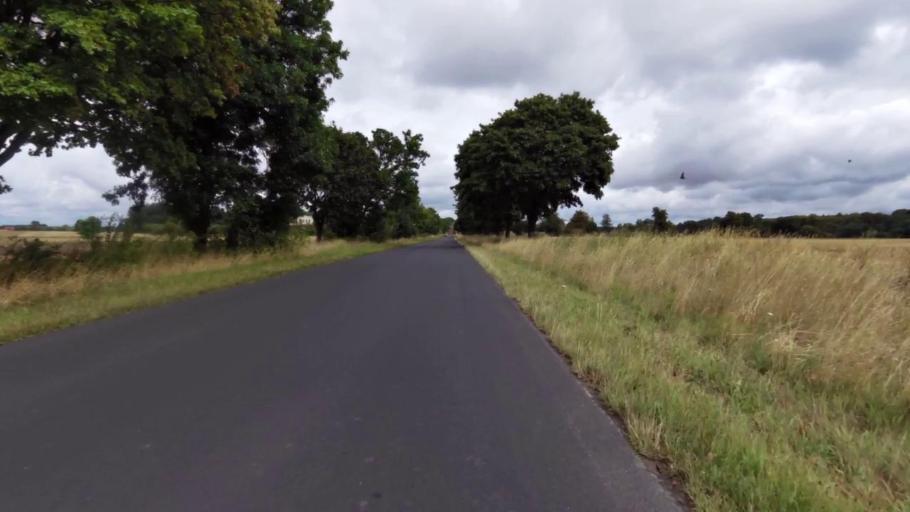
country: PL
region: West Pomeranian Voivodeship
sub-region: Powiat mysliborski
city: Debno
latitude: 52.8433
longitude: 14.6728
